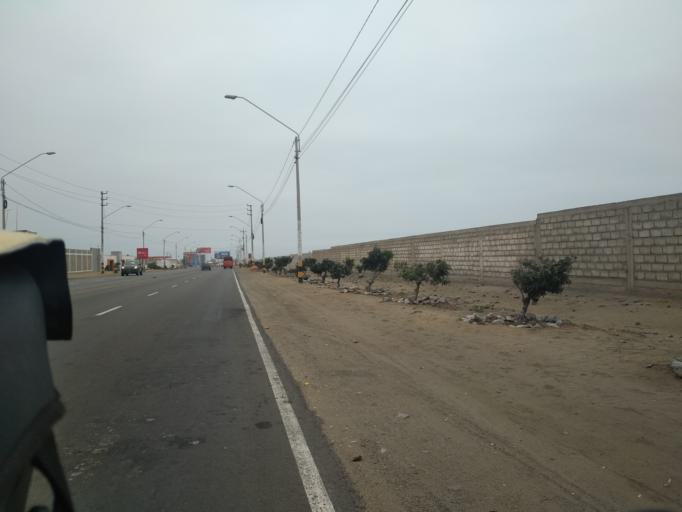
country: PE
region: La Libertad
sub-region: Provincia de Trujillo
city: Huanchaco
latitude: -8.0934
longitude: -79.1063
